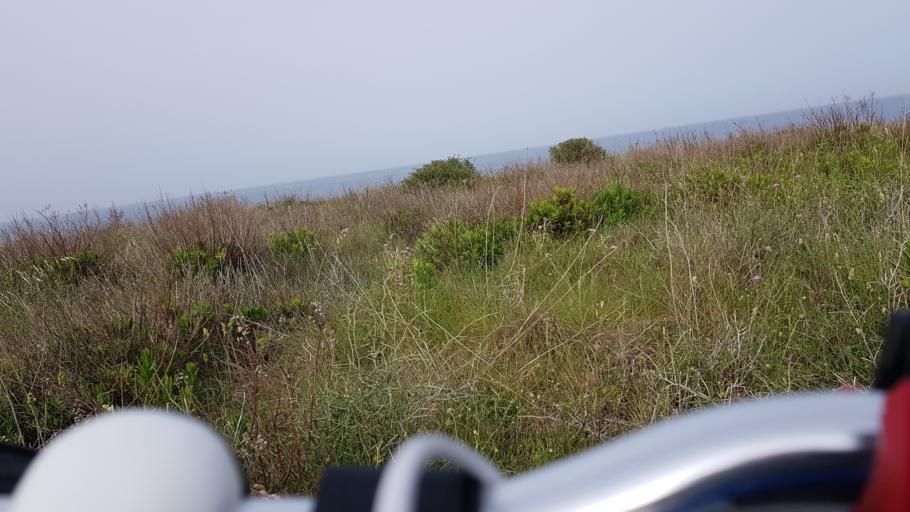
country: IT
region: Apulia
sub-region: Provincia di Brindisi
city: La Rosa
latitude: 40.5836
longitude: 18.0418
